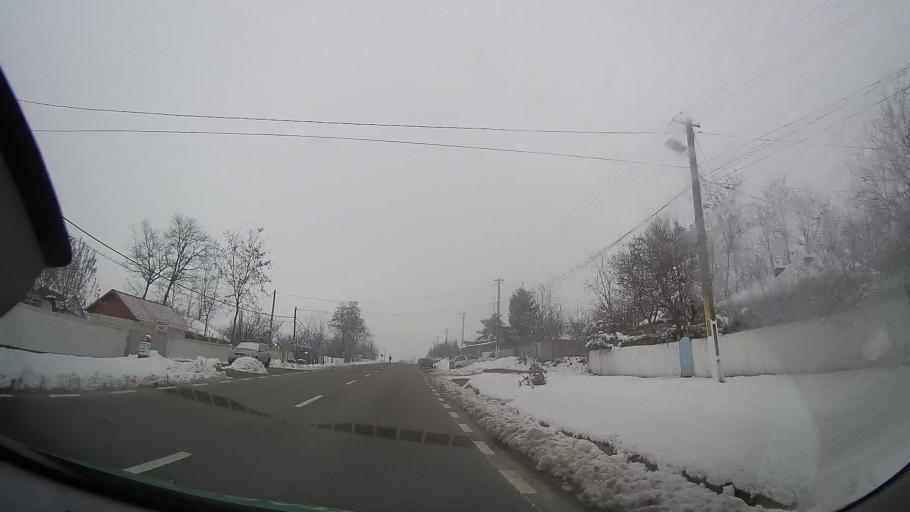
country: RO
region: Vaslui
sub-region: Comuna Stefan cel Mare
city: Stefan cel Mare
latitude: 46.7249
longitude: 27.6212
